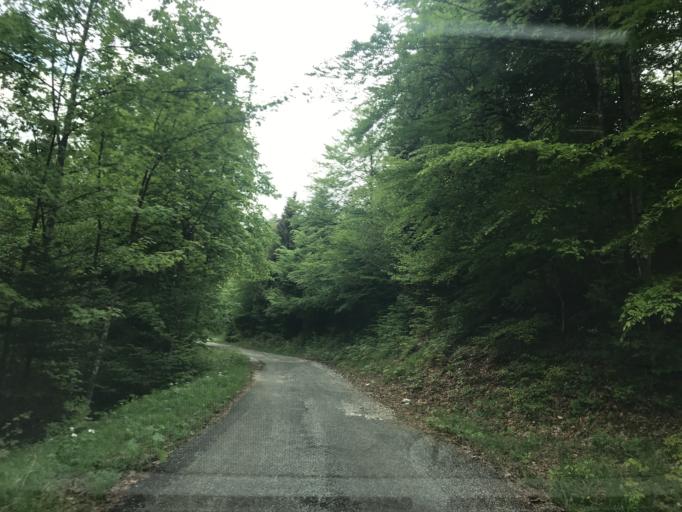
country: FR
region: Rhone-Alpes
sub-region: Departement de la Savoie
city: La Motte-Servolex
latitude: 45.6026
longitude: 5.8222
